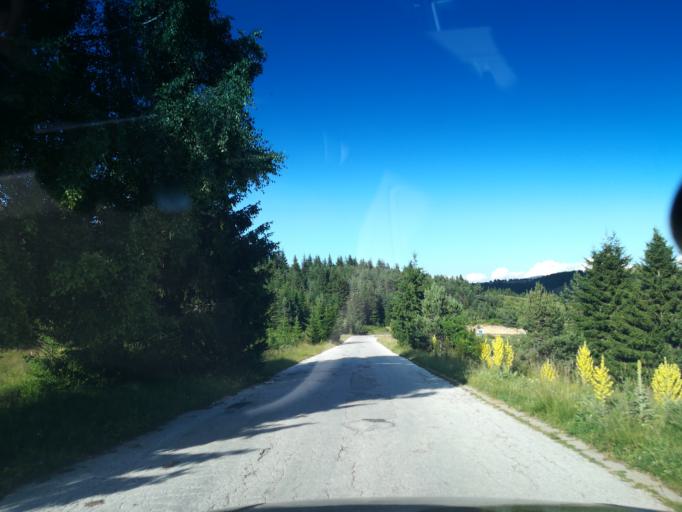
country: BG
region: Smolyan
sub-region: Obshtina Chepelare
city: Chepelare
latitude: 41.6974
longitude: 24.7764
